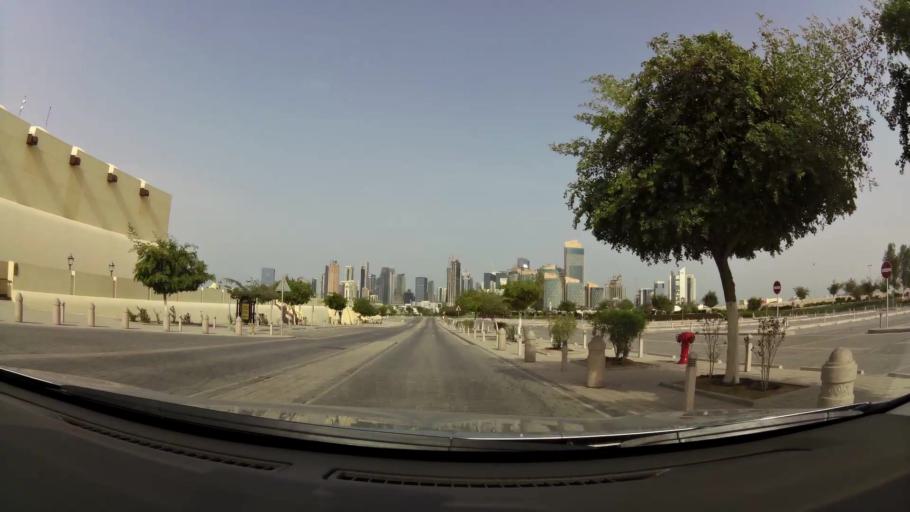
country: QA
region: Baladiyat ad Dawhah
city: Doha
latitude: 25.3163
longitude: 51.5055
